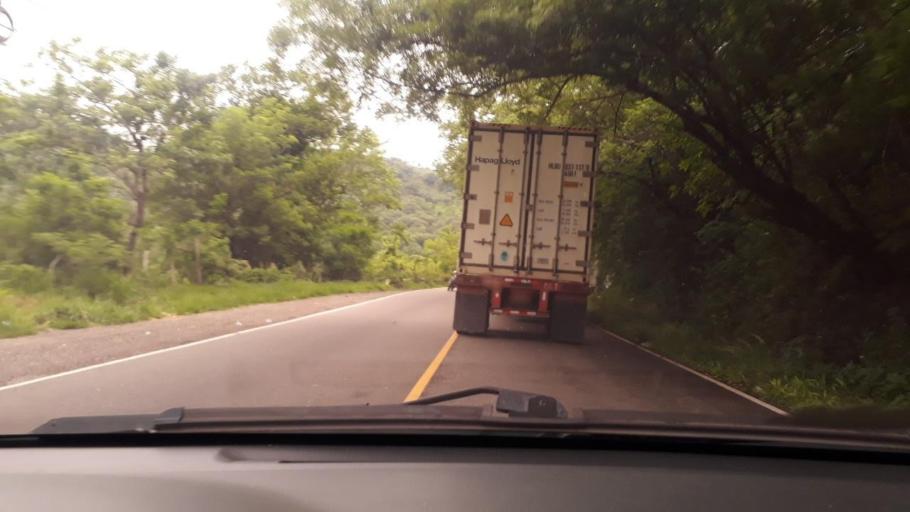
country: GT
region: Chiquimula
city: Quezaltepeque
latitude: 14.6054
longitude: -89.4522
